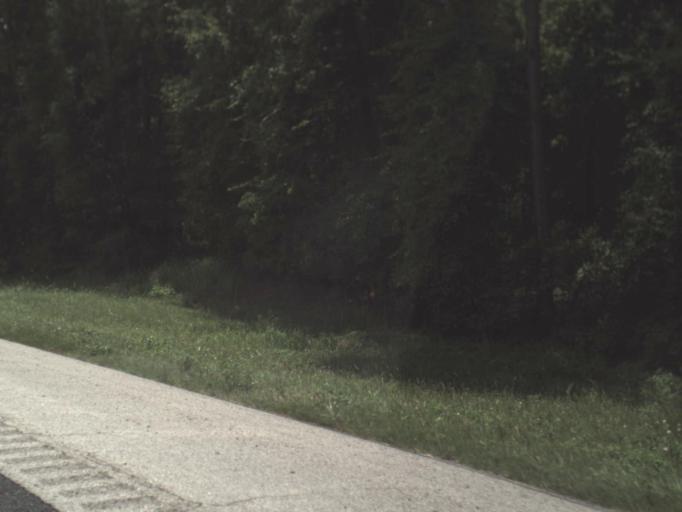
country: US
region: Florida
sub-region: Alachua County
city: High Springs
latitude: 29.8496
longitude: -82.5343
